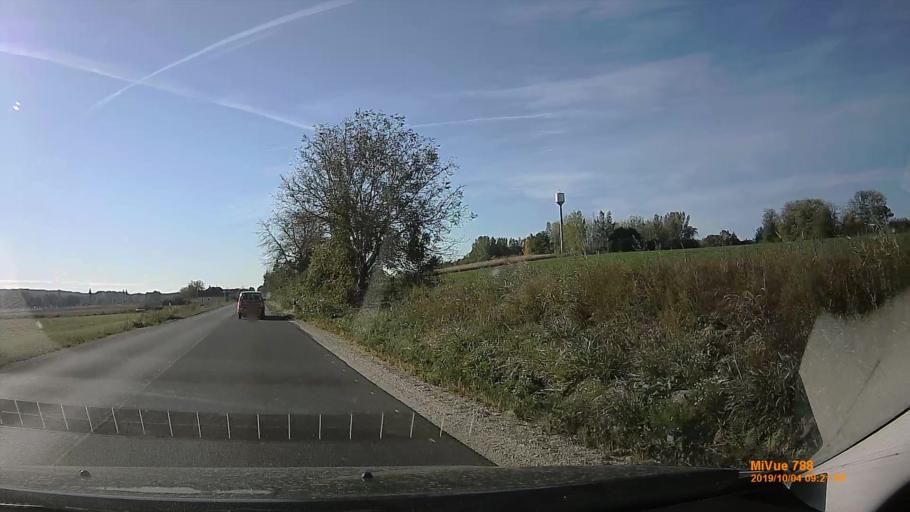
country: HU
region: Somogy
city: Karad
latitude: 46.5580
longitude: 17.8103
